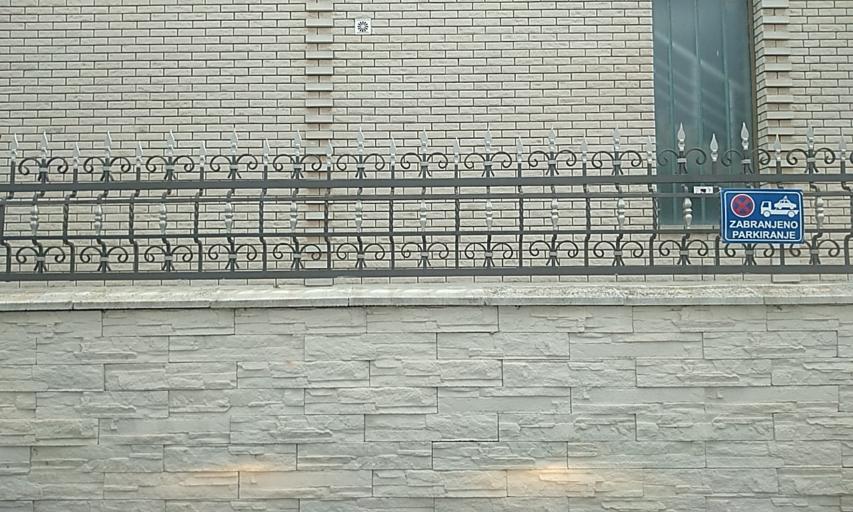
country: RS
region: Central Serbia
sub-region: Nisavski Okrug
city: Nis
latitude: 43.3244
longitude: 21.9459
